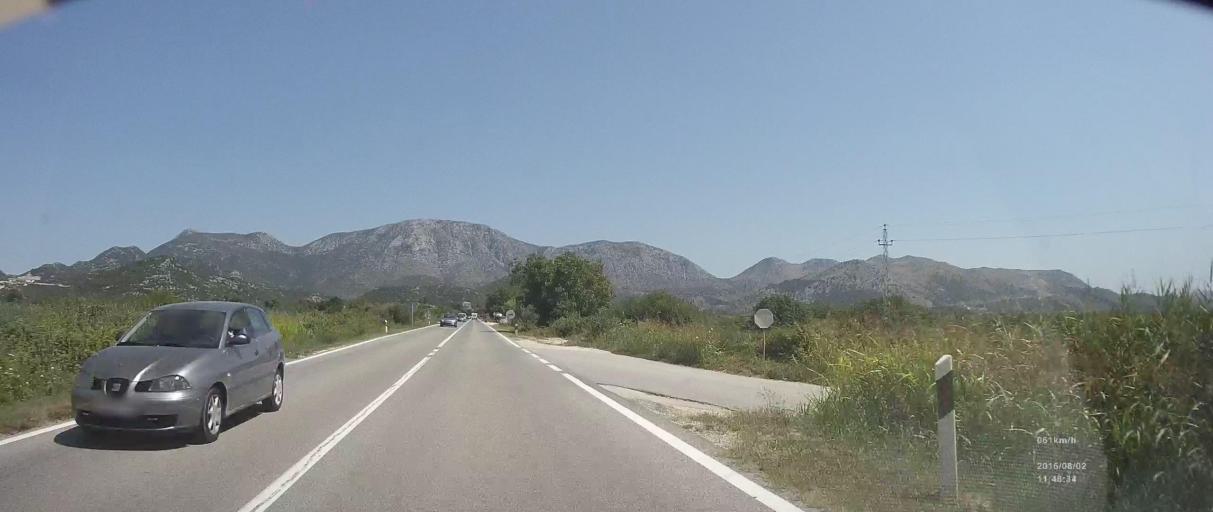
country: HR
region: Dubrovacko-Neretvanska
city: Komin
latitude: 43.0356
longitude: 17.4906
